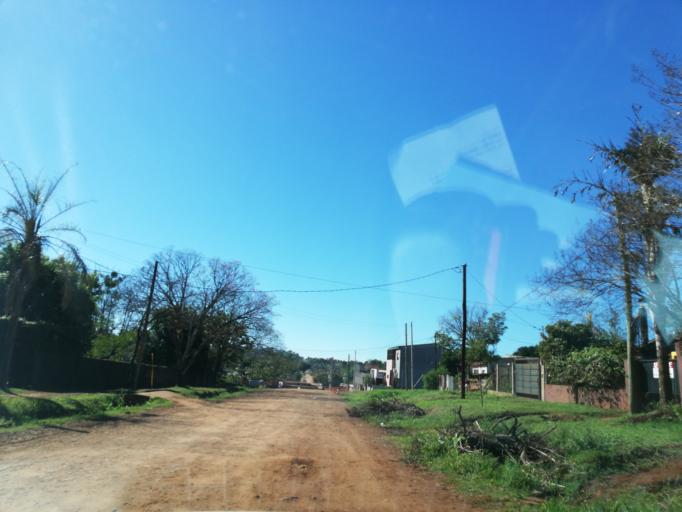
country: AR
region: Misiones
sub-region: Departamento de Capital
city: Posadas
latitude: -27.3933
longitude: -55.9418
